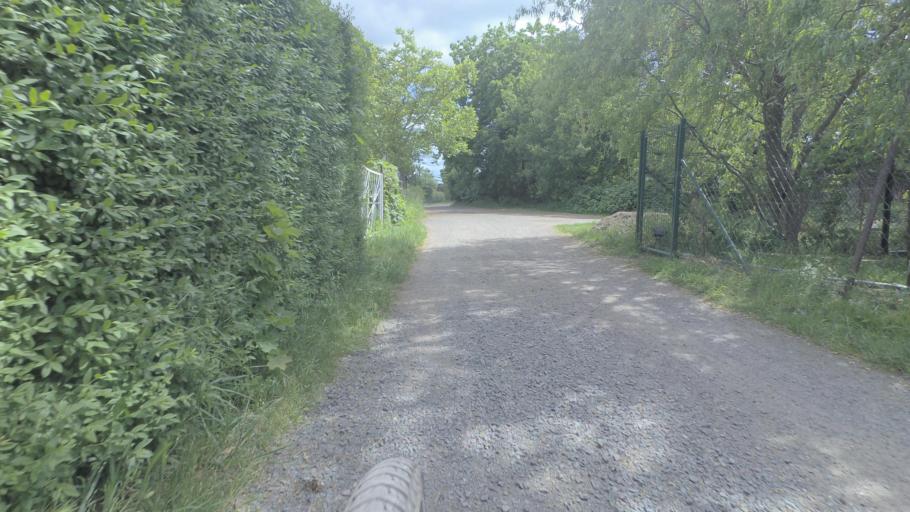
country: DE
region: Brandenburg
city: Falkensee
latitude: 52.5650
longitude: 13.0978
